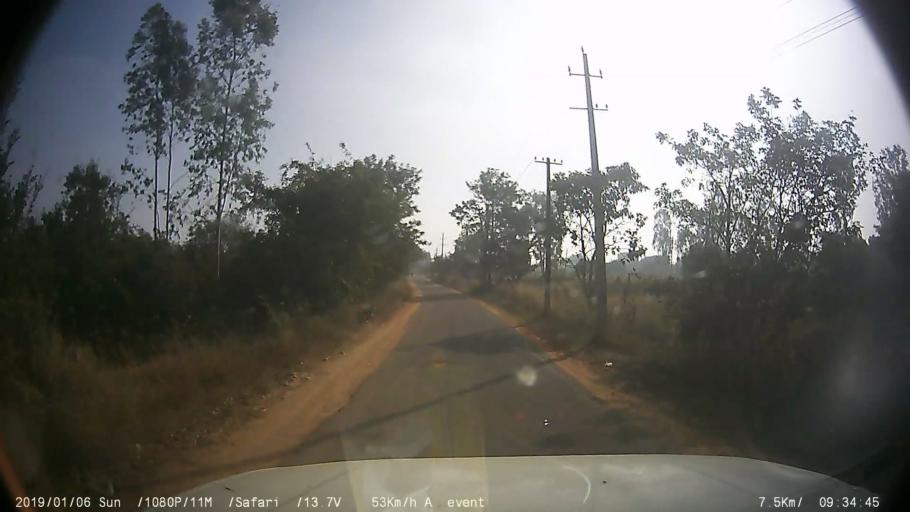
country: IN
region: Karnataka
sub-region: Bangalore Urban
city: Anekal
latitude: 12.8196
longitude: 77.6470
